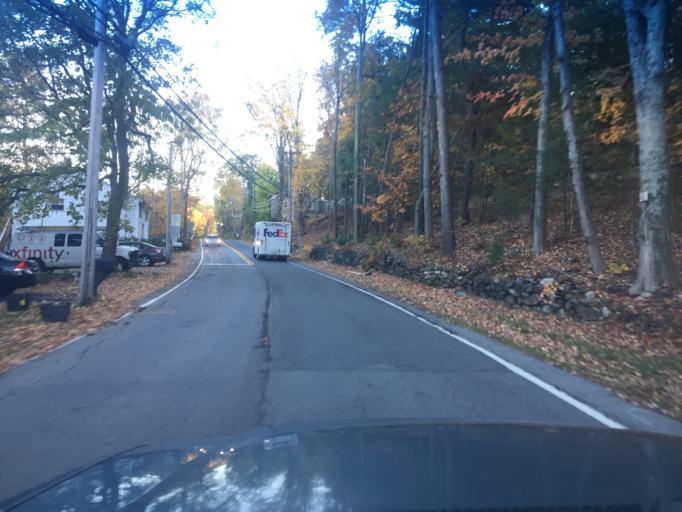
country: US
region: Massachusetts
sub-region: Middlesex County
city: Stow
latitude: 42.4043
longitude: -71.5267
